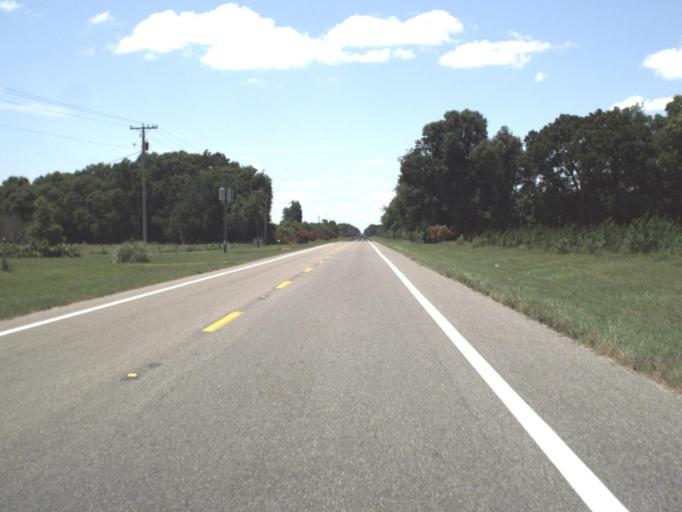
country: US
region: Florida
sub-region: Lafayette County
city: Mayo
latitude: 29.9979
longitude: -83.0170
